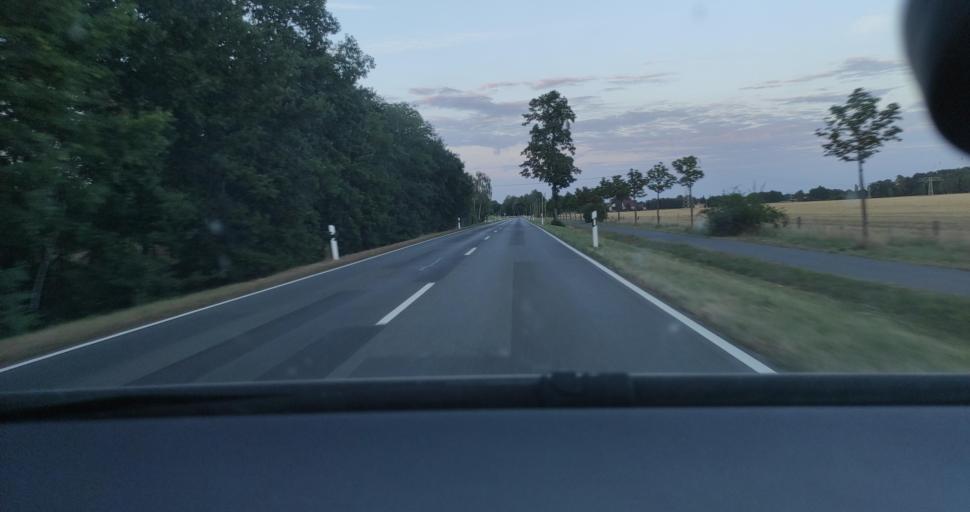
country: DE
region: Brandenburg
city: Forst
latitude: 51.7224
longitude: 14.5983
